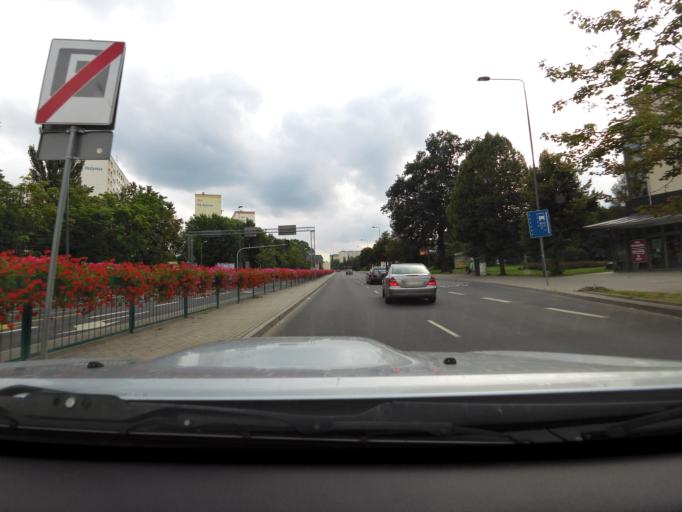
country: PL
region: Warmian-Masurian Voivodeship
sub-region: Powiat olsztynski
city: Olsztyn
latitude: 53.7730
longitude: 20.4756
